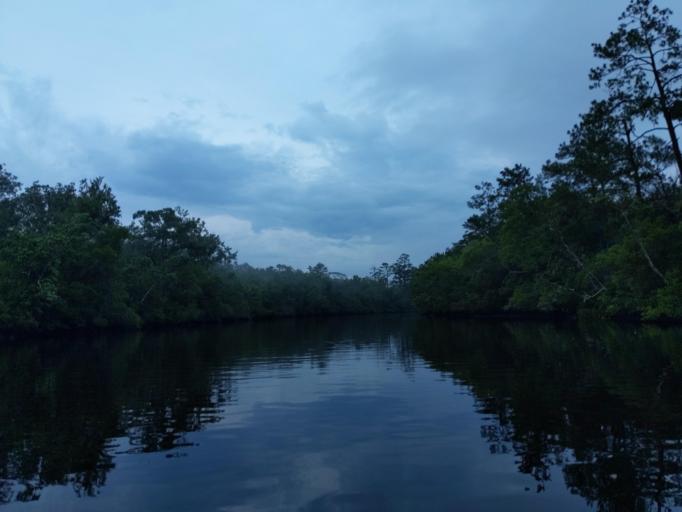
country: US
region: Florida
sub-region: Wakulla County
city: Crawfordville
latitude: 30.0336
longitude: -84.5131
